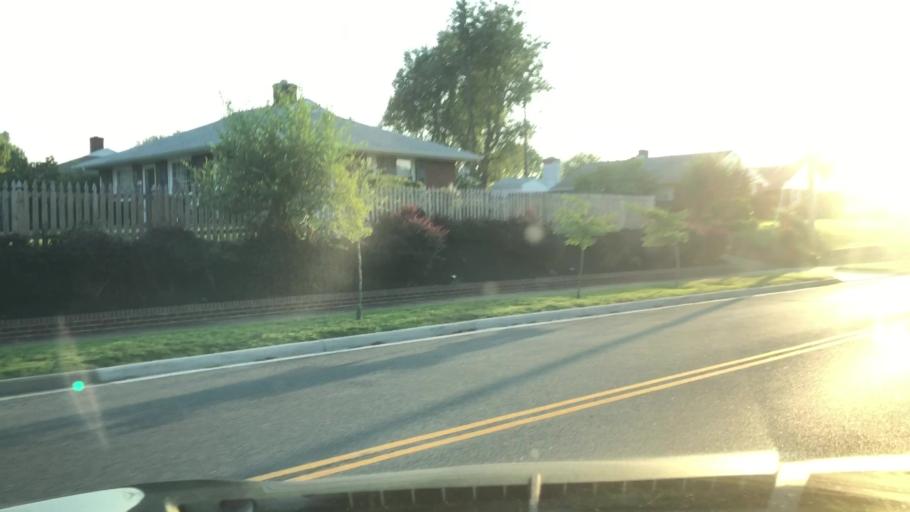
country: US
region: Virginia
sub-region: Stafford County
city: Falmouth
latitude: 38.3157
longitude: -77.4779
